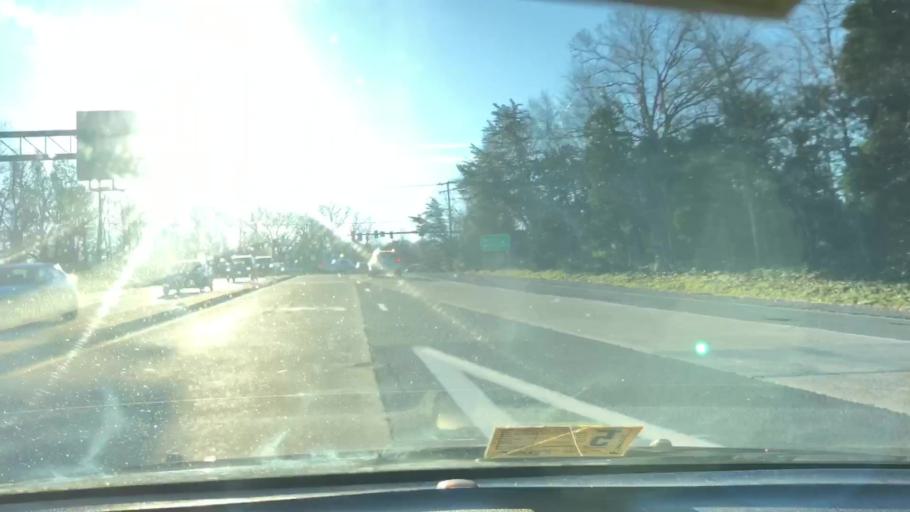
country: US
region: Virginia
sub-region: Fairfax County
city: Franconia
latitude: 38.7949
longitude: -77.1383
